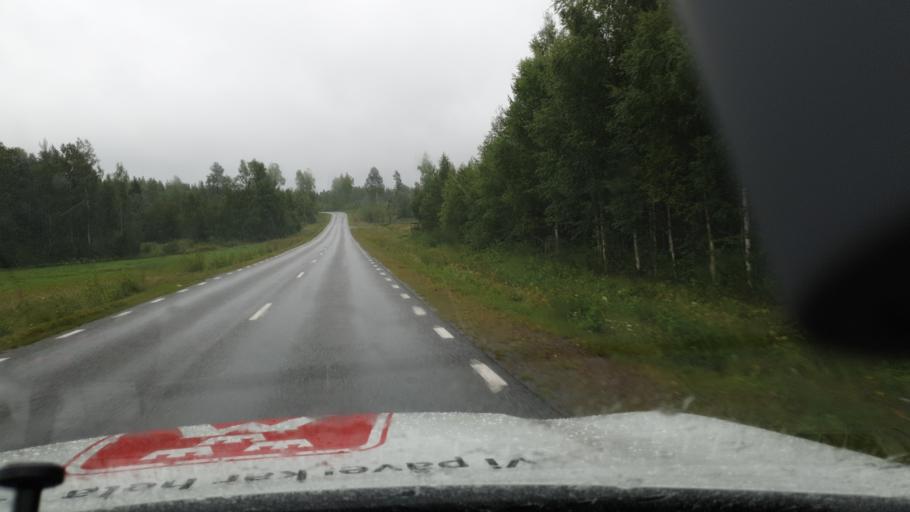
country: SE
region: Vaesterbotten
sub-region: Skelleftea Kommun
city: Viken
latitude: 64.6707
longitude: 20.8767
